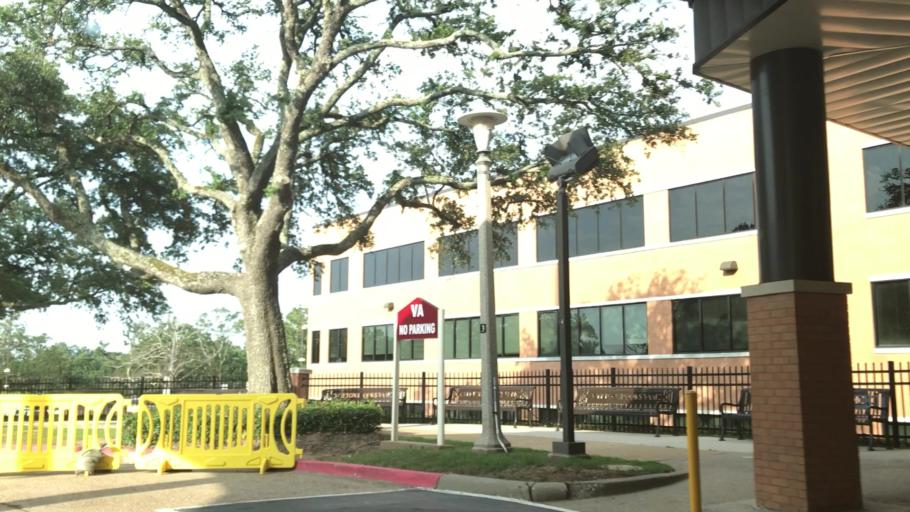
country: US
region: Louisiana
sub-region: Bossier Parish
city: Bossier City
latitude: 32.5028
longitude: -93.7215
